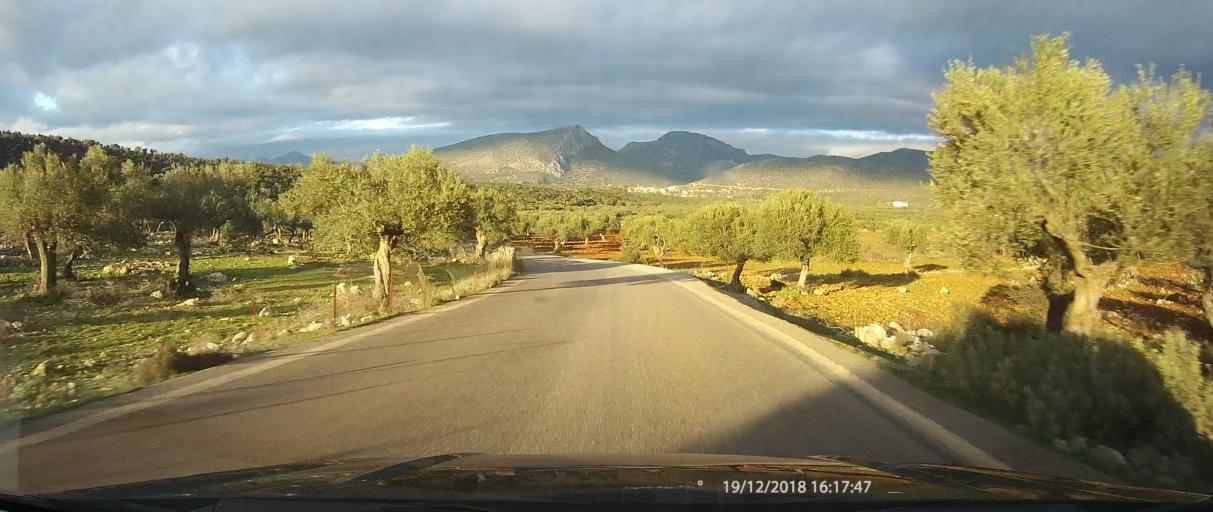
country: GR
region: Peloponnese
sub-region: Nomos Lakonias
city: Kato Glikovrisi
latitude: 36.9155
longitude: 22.8117
